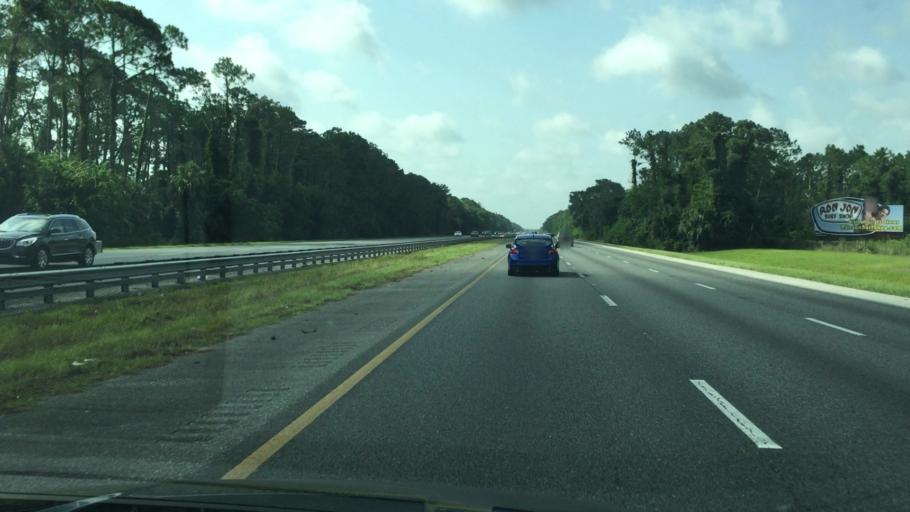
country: US
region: Florida
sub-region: Volusia County
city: Ormond-by-the-Sea
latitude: 29.3799
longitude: -81.1449
